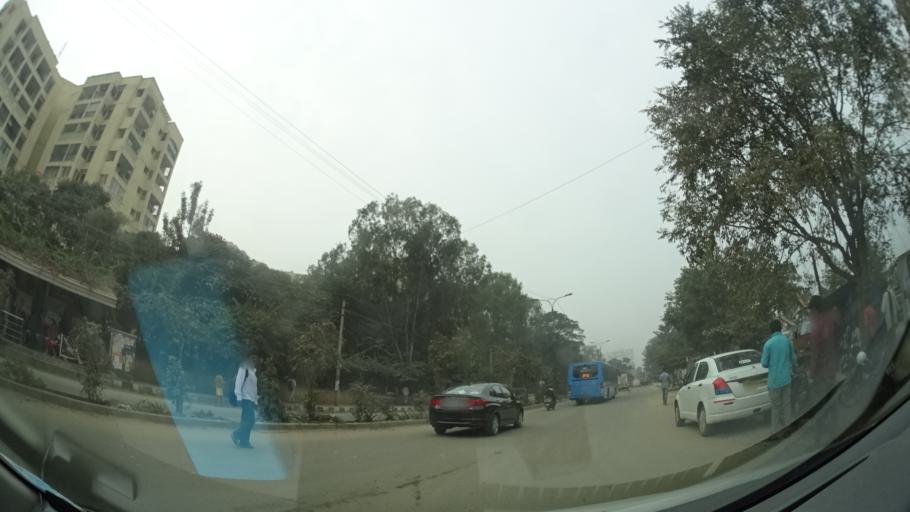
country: IN
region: Karnataka
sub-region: Bangalore Rural
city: Hoskote
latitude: 12.9918
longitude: 77.7154
